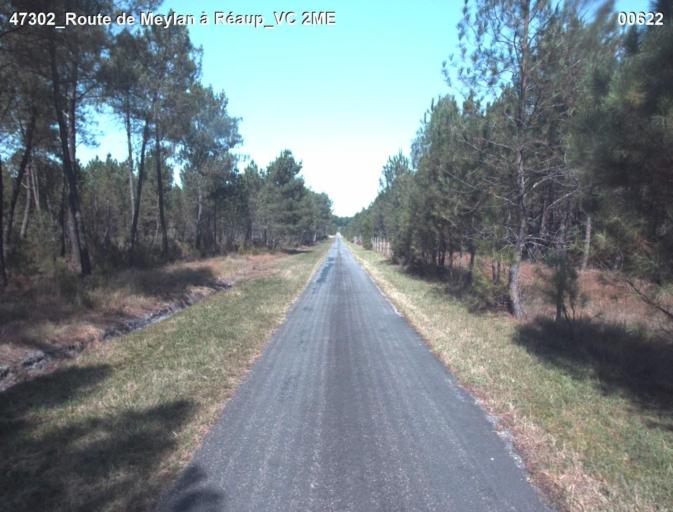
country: FR
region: Aquitaine
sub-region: Departement du Lot-et-Garonne
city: Mezin
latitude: 44.1028
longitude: 0.1373
